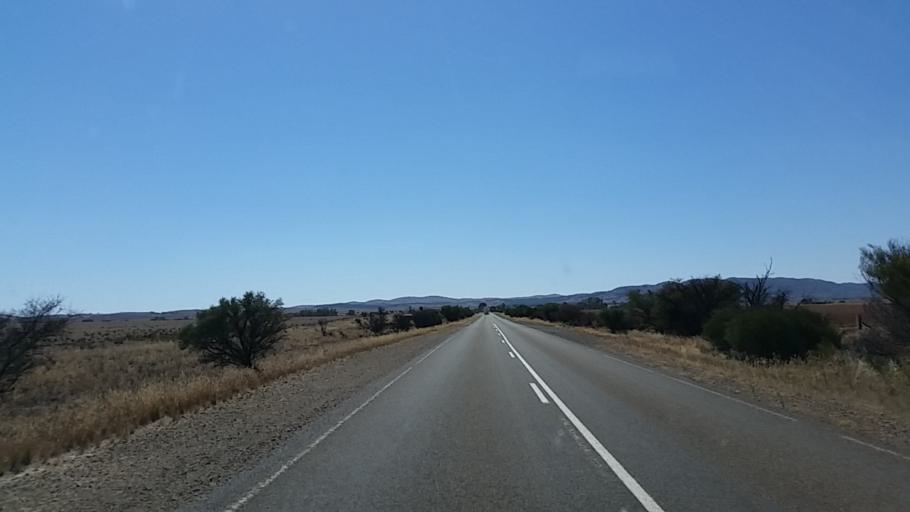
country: AU
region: South Australia
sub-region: Peterborough
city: Peterborough
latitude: -32.6477
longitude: 138.6005
